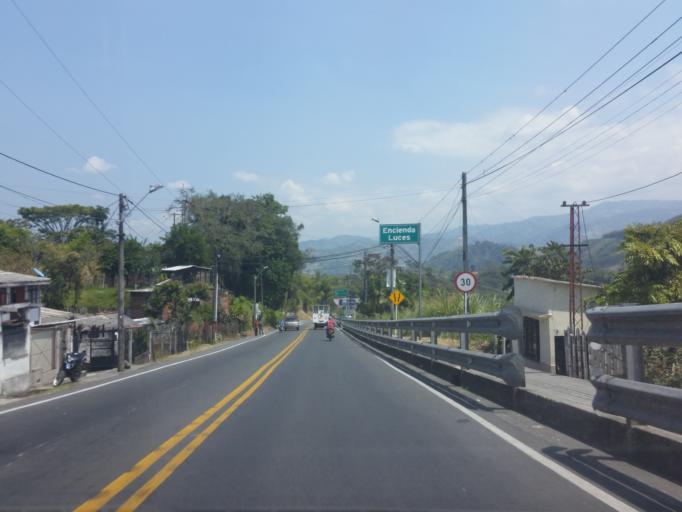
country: CO
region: Caldas
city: Chinchina
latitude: 4.9893
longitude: -75.6054
